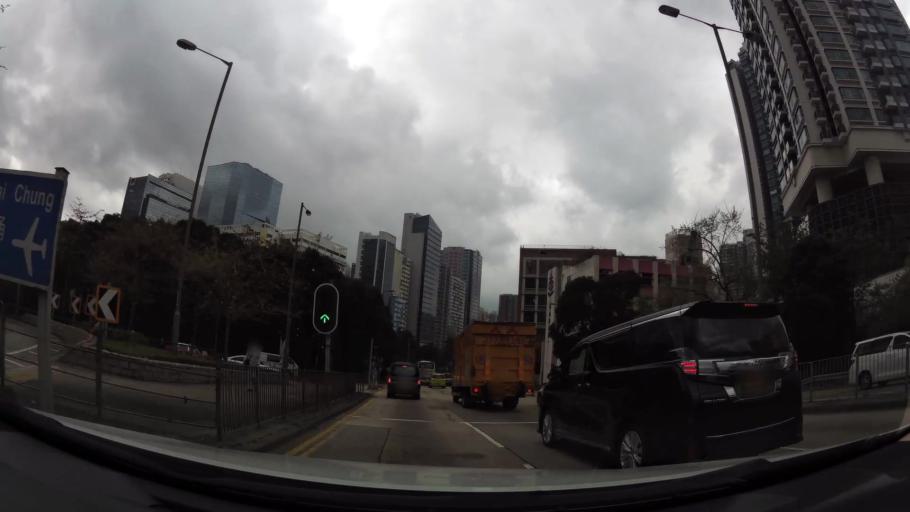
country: HK
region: Wong Tai Sin
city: Wong Tai Sin
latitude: 22.3409
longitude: 114.1984
